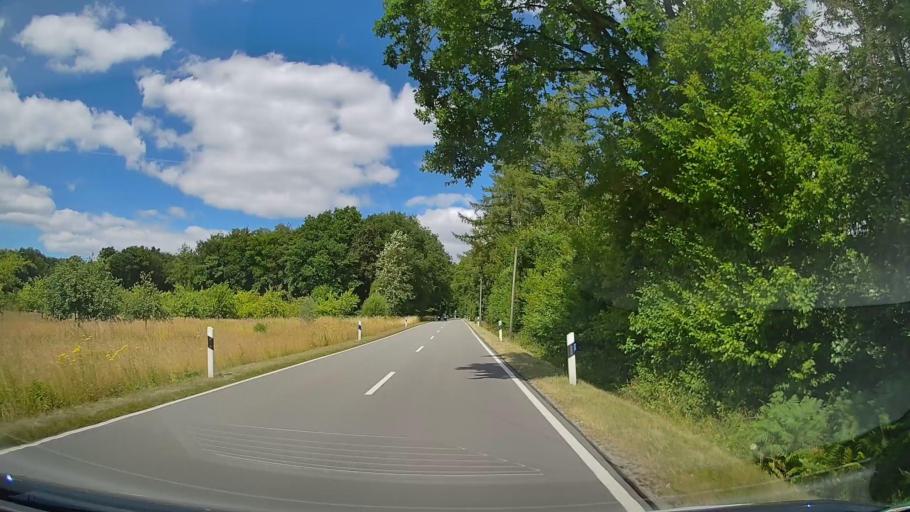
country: DE
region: Lower Saxony
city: Belm
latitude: 52.3557
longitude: 8.1446
